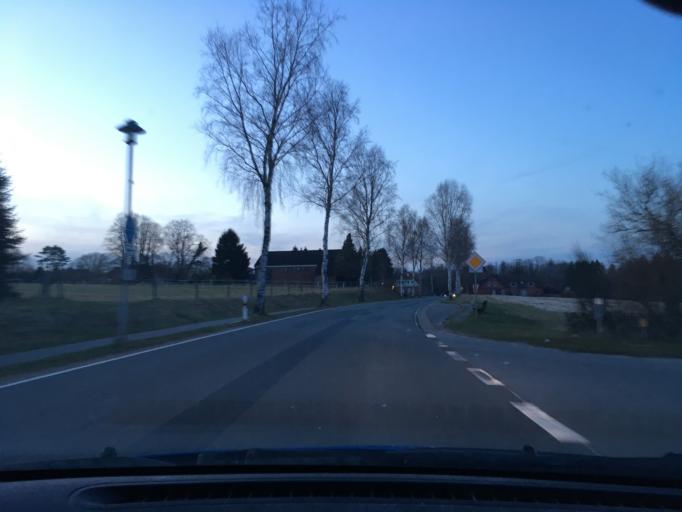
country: DE
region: Lower Saxony
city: Egestorf
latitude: 53.1863
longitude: 10.0623
